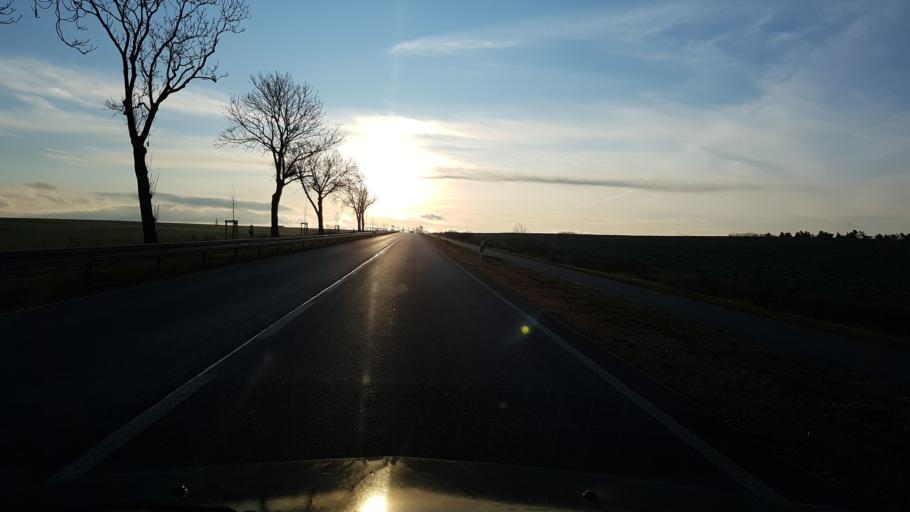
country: DE
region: Saxony
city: Radibor
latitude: 51.2336
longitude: 14.3738
